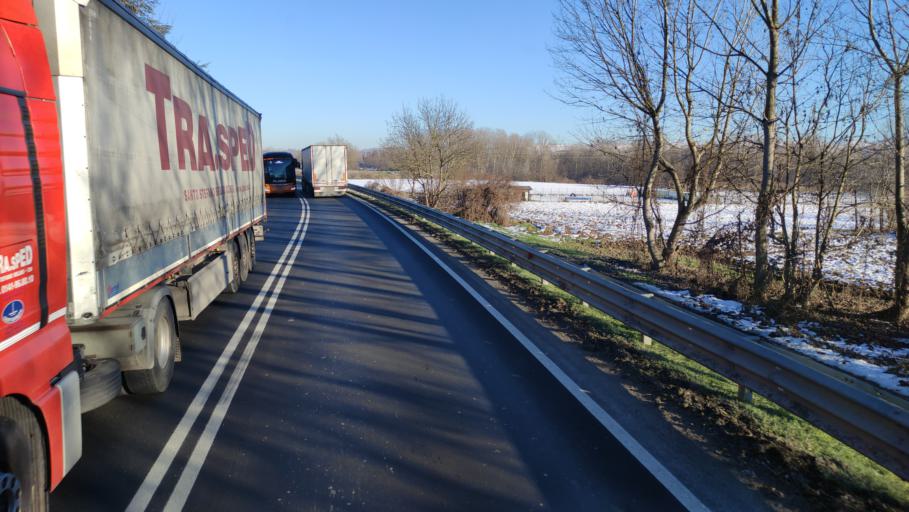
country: IT
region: Piedmont
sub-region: Provincia di Cuneo
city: Mussotto
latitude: 44.7090
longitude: 8.0046
